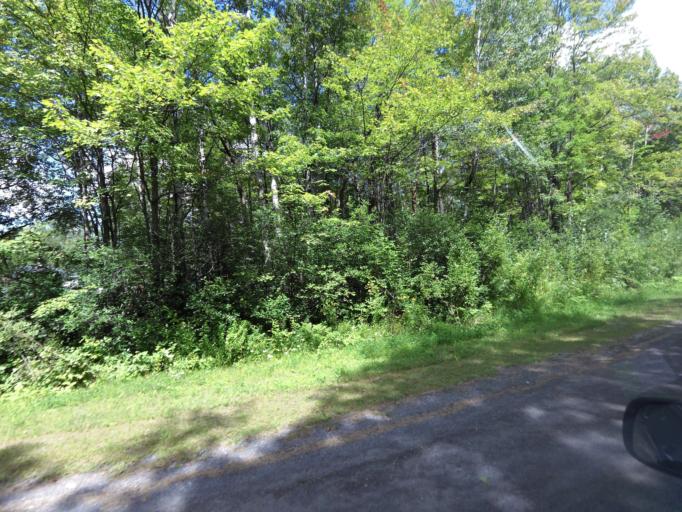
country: CA
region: Ontario
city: Ottawa
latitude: 45.4186
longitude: -75.5574
